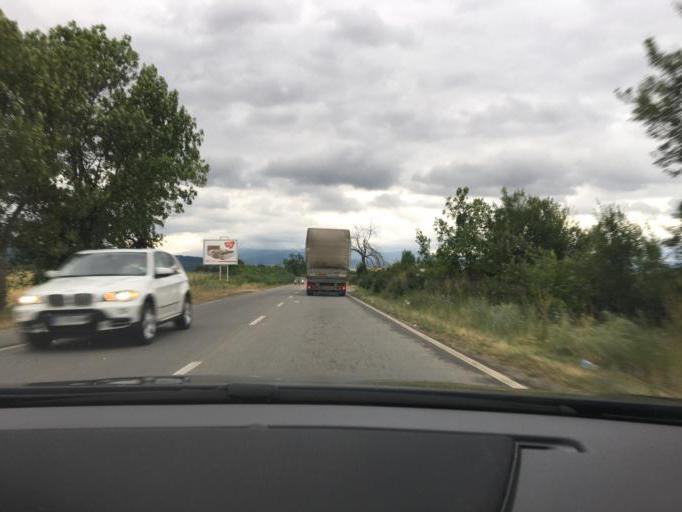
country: BG
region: Kyustendil
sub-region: Obshtina Kyustendil
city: Kyustendil
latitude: 42.2730
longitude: 22.7664
